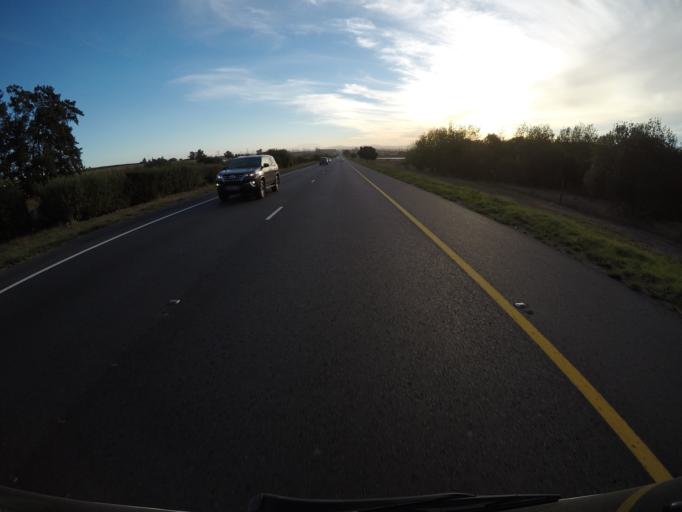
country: ZA
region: Western Cape
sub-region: City of Cape Town
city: Kraaifontein
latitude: -33.8126
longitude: 18.8171
